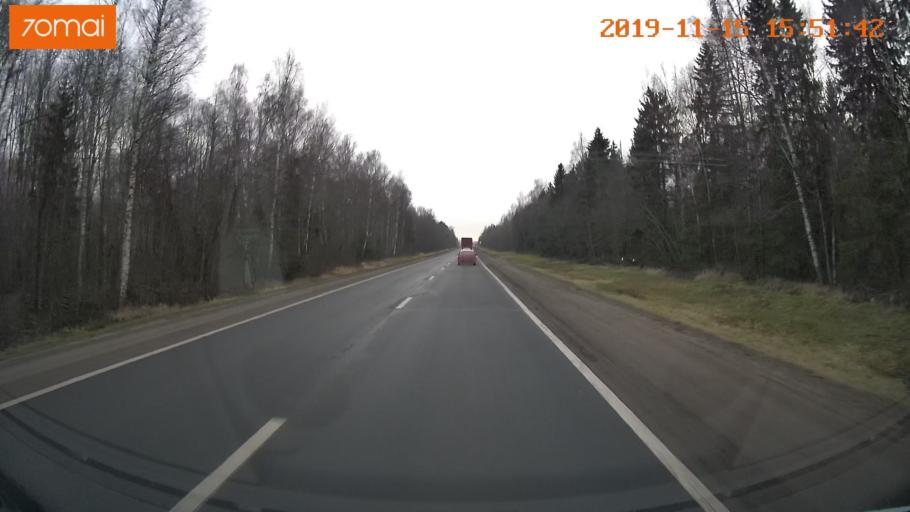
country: RU
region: Jaroslavl
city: Yaroslavl
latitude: 57.8914
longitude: 40.0055
